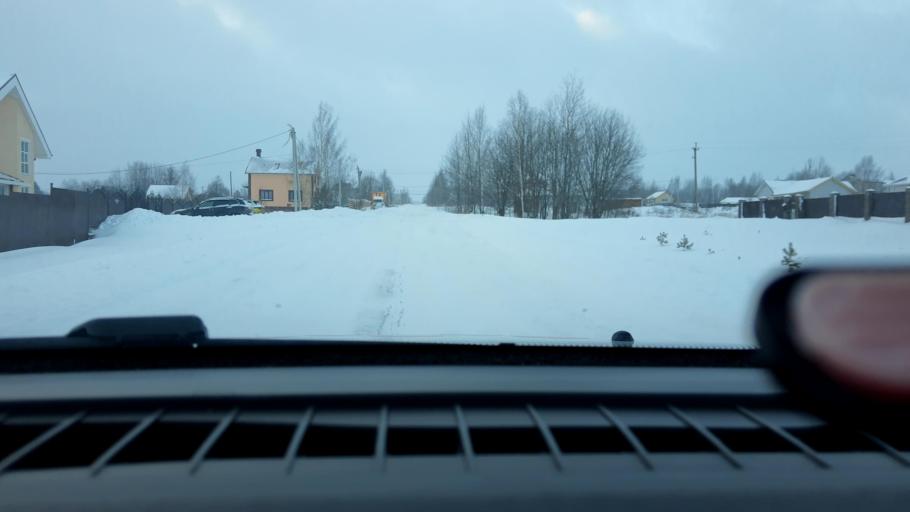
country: RU
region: Nizjnij Novgorod
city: Burevestnik
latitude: 56.1500
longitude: 43.7617
